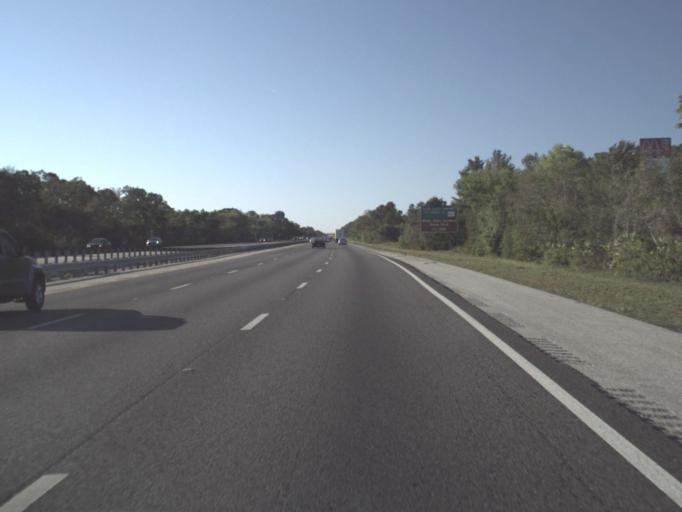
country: US
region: Florida
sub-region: Flagler County
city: Palm Coast
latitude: 29.5359
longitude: -81.2067
